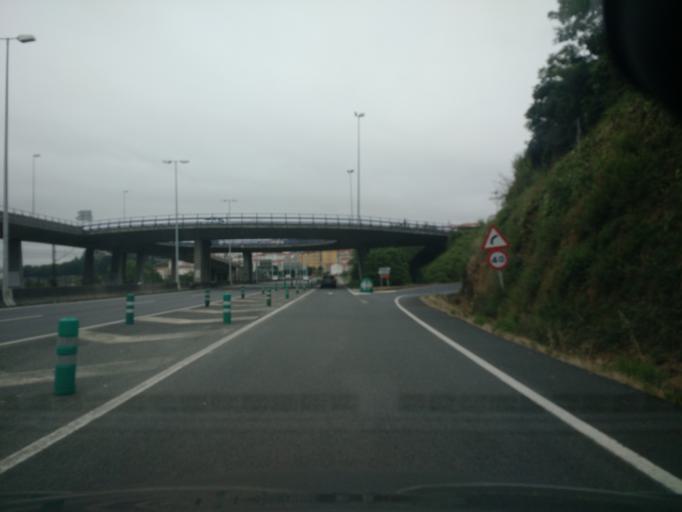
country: ES
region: Galicia
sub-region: Provincia da Coruna
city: Santiago de Compostela
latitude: 42.8790
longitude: -8.5258
